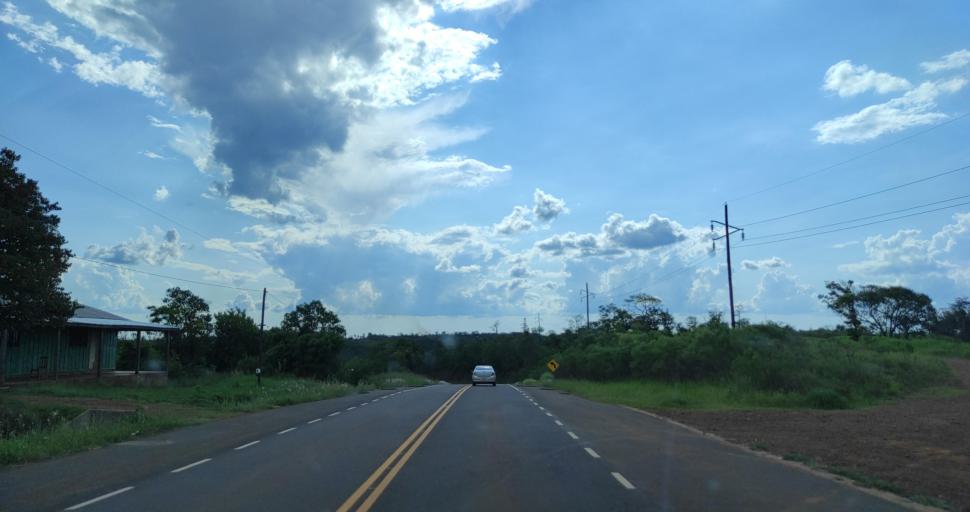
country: AR
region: Misiones
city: Bernardo de Irigoyen
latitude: -26.2985
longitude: -53.8114
